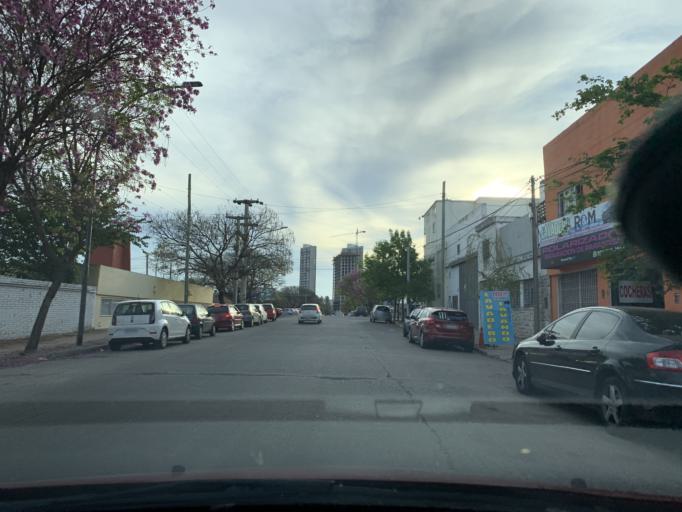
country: AR
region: Cordoba
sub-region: Departamento de Capital
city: Cordoba
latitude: -31.4083
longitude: -64.1673
